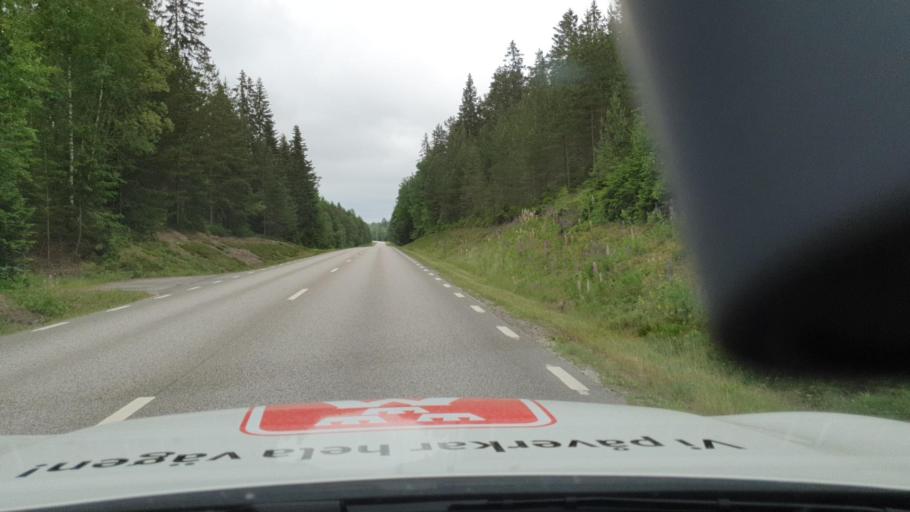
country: SE
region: Vaestra Goetaland
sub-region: Tibro Kommun
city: Tibro
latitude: 58.3747
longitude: 14.2035
